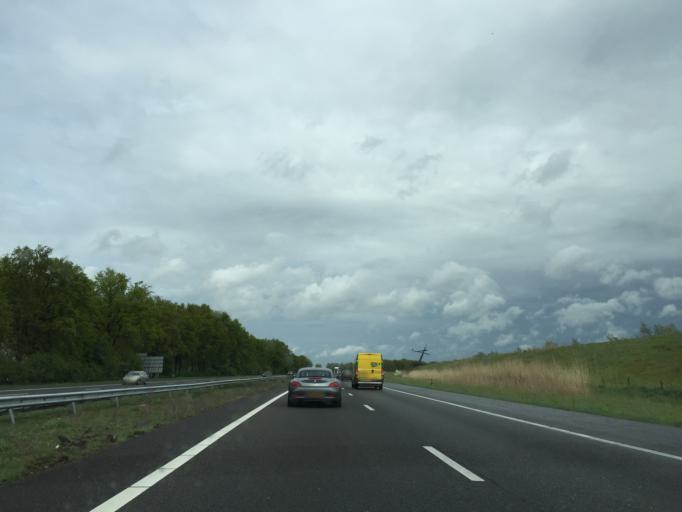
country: NL
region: Gelderland
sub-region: Gemeente Ermelo
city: Horst
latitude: 52.3252
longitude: 5.5768
